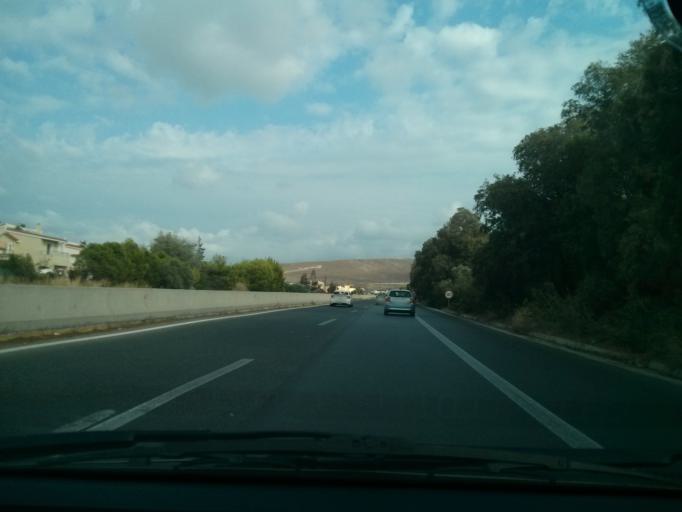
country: GR
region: Crete
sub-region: Nomos Irakleiou
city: Kokkini Hani
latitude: 35.3299
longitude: 25.2454
